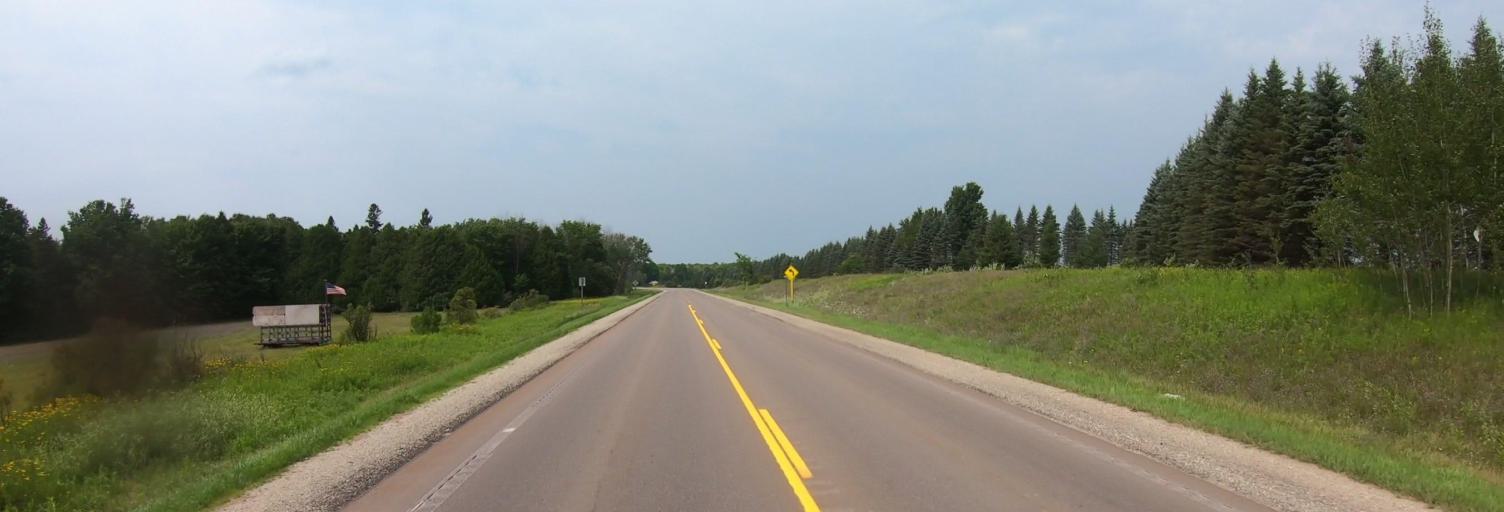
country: US
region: Michigan
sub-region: Alger County
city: Munising
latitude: 46.3502
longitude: -86.9513
